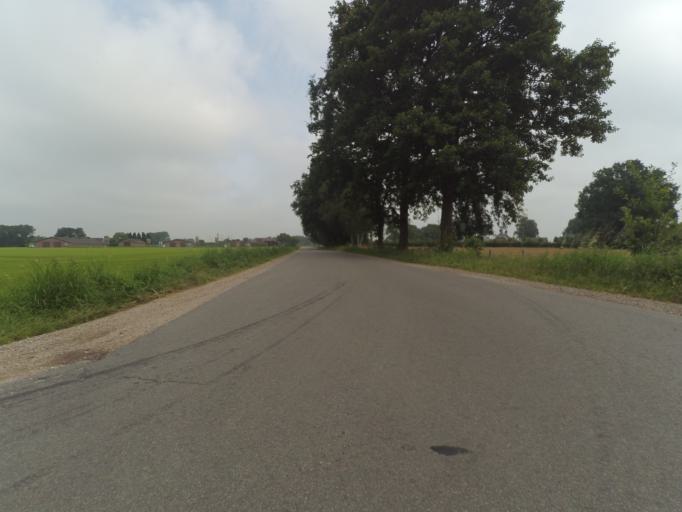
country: NL
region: Gelderland
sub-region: Gemeente Barneveld
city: Kootwijkerbroek
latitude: 52.1407
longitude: 5.6647
